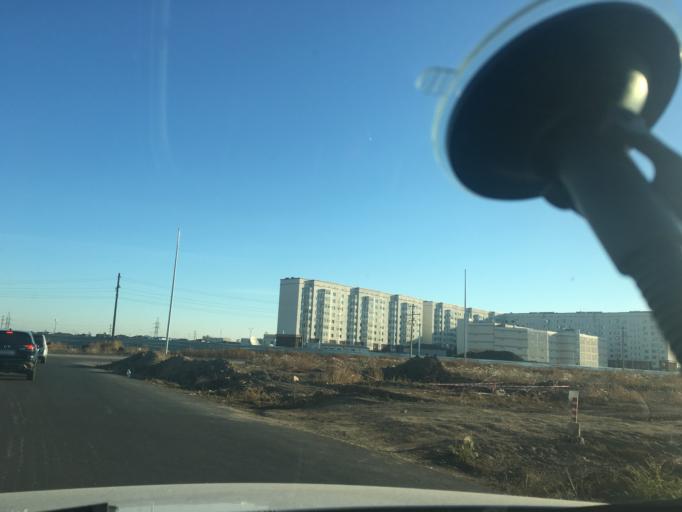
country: KZ
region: Astana Qalasy
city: Astana
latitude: 51.1423
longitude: 71.3714
